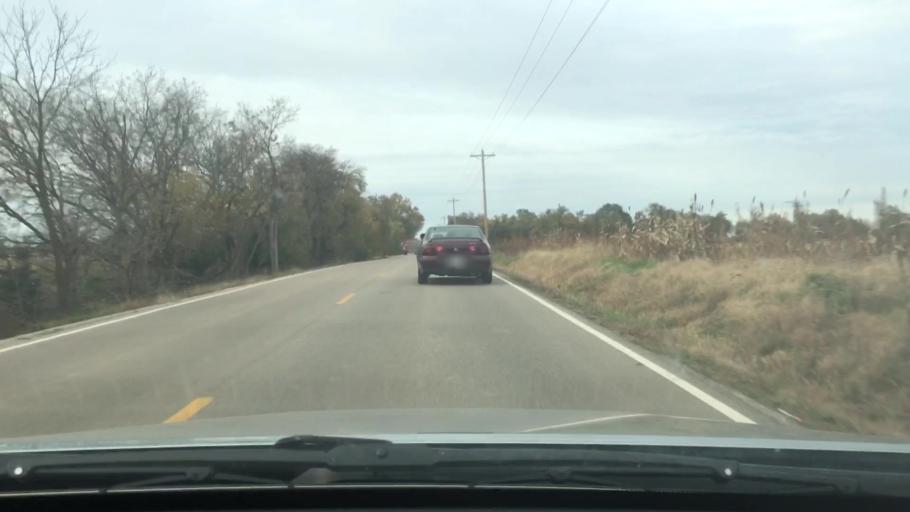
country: US
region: Kansas
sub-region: Sedgwick County
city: Maize
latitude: 37.7590
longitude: -97.4992
